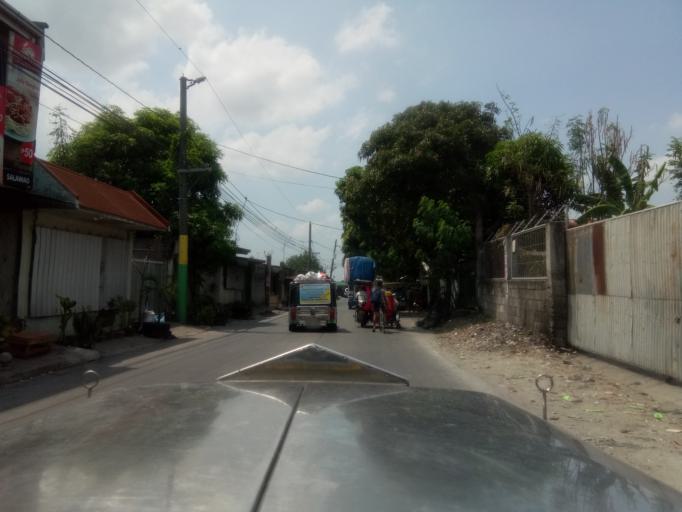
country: PH
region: Calabarzon
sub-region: Province of Cavite
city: Dasmarinas
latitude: 14.3182
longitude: 120.9763
